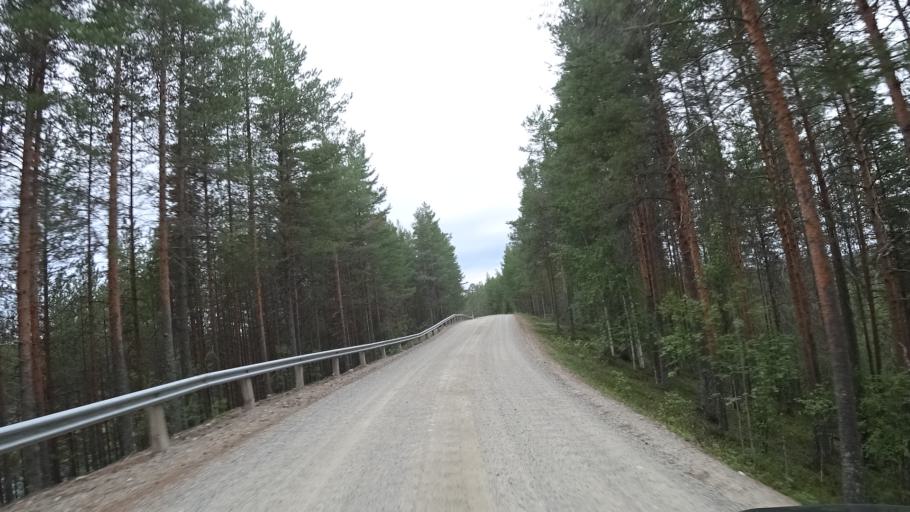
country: FI
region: North Karelia
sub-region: Pielisen Karjala
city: Lieksa
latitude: 63.2346
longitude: 30.3643
